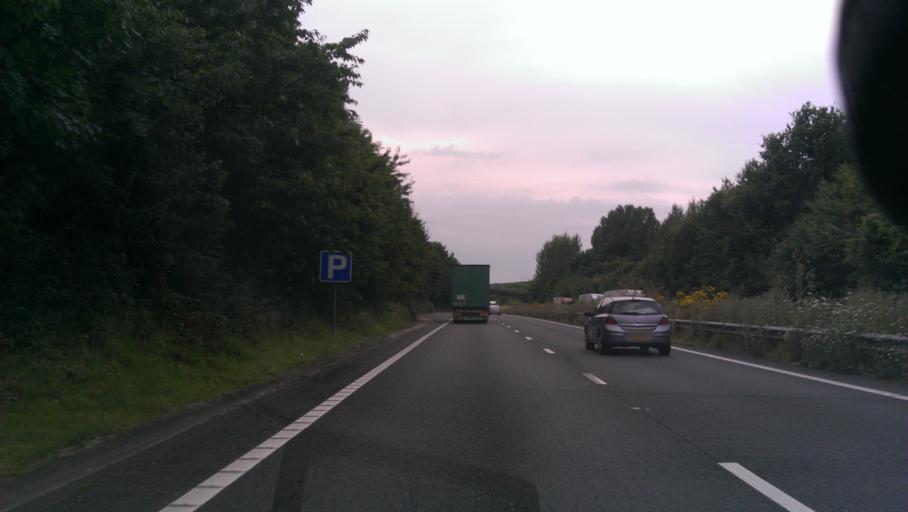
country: GB
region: England
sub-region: Kent
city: Blean
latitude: 51.2786
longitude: 1.0435
